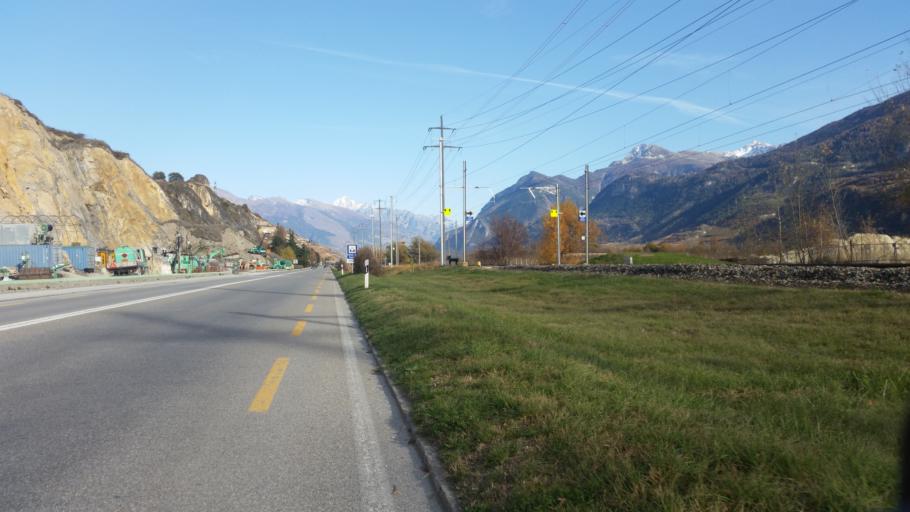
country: CH
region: Valais
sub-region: Sierre District
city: Grone
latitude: 46.2574
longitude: 7.4363
